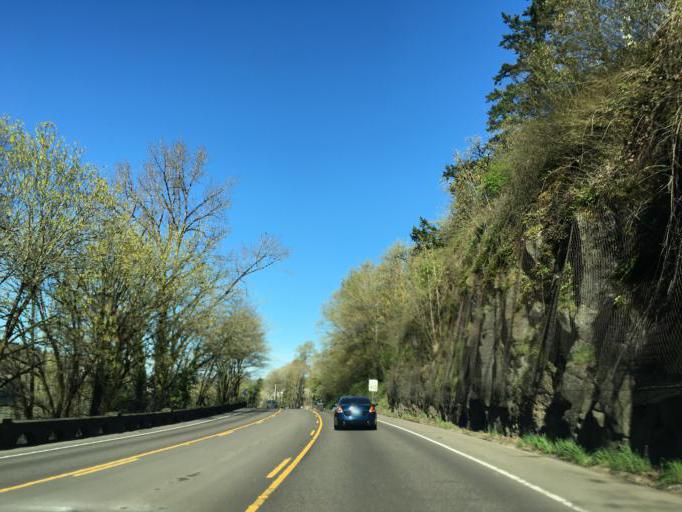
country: US
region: Oregon
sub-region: Clackamas County
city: Oregon City
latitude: 45.3447
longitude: -122.6292
